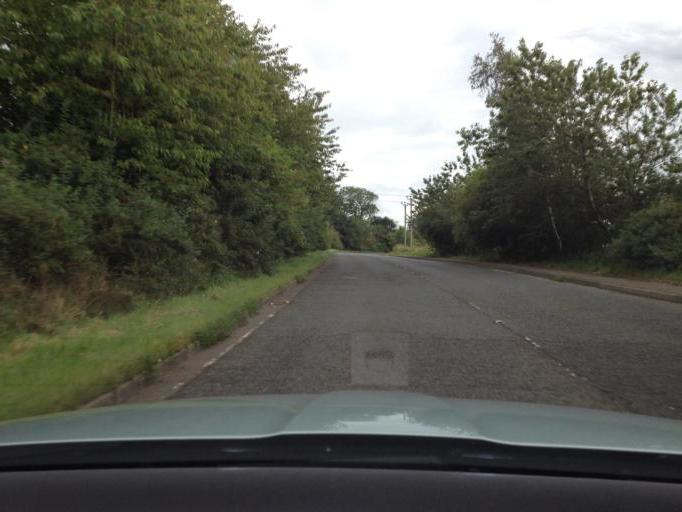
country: GB
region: Scotland
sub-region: West Lothian
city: Bathgate
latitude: 55.9175
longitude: -3.6446
